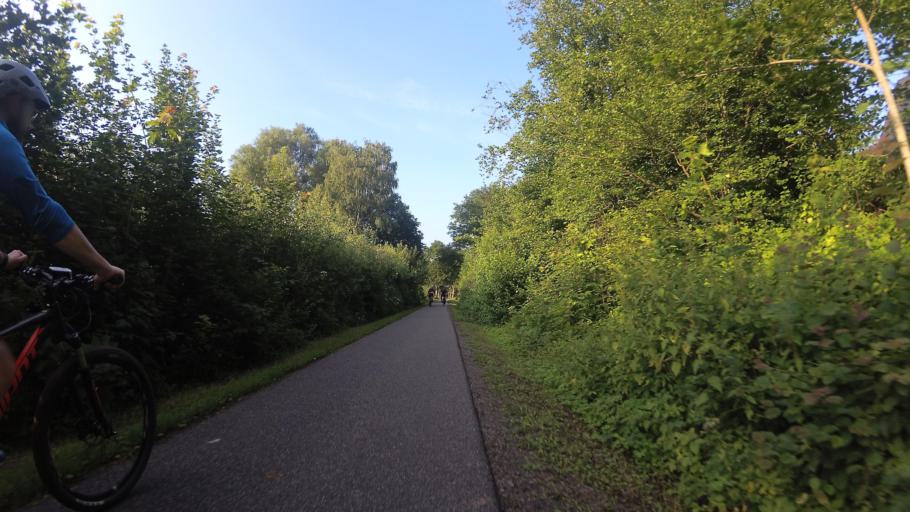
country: DE
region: Rheinland-Pfalz
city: Althornbach
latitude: 49.2159
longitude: 7.3690
